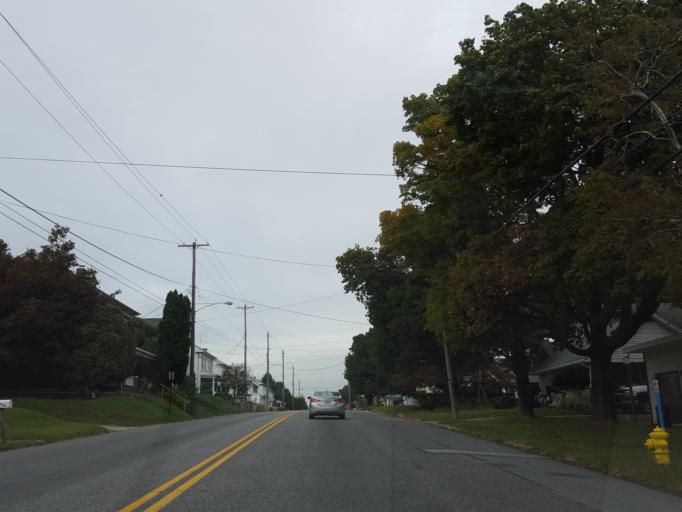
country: US
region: Pennsylvania
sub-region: York County
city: Weigelstown
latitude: 39.9288
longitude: -76.8431
